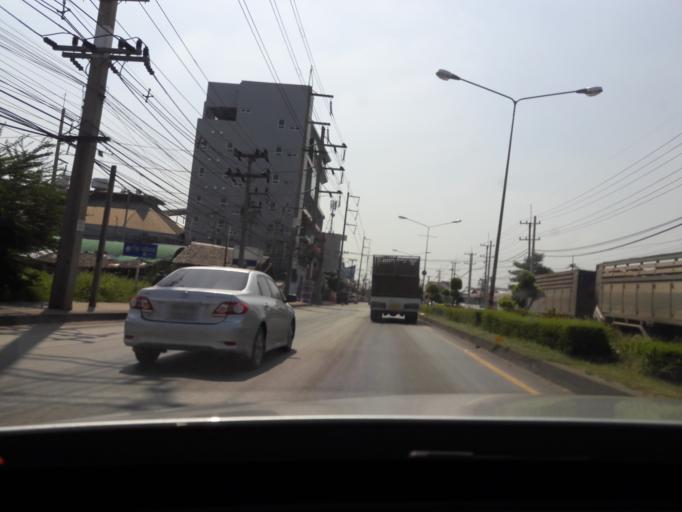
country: TH
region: Samut Sakhon
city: Samut Sakhon
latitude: 13.5815
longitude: 100.2772
